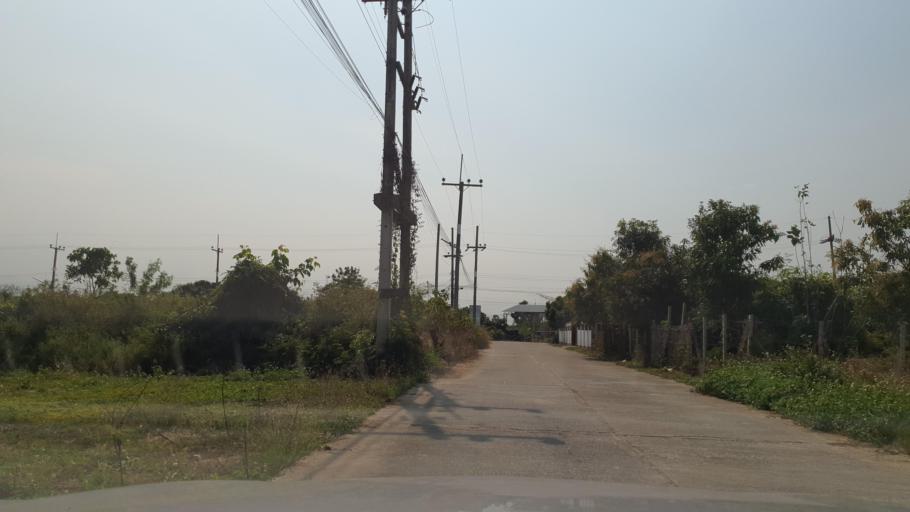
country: TH
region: Chiang Mai
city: San Pa Tong
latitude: 18.6516
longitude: 98.8910
